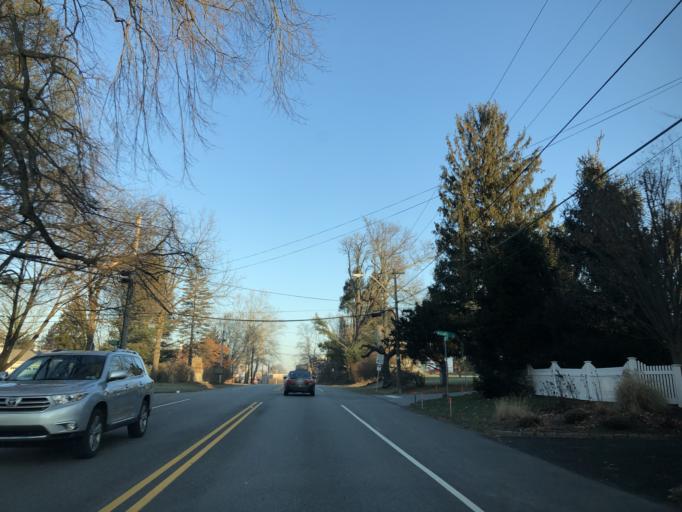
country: US
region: Pennsylvania
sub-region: Chester County
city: West Chester
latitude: 39.9477
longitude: -75.5935
